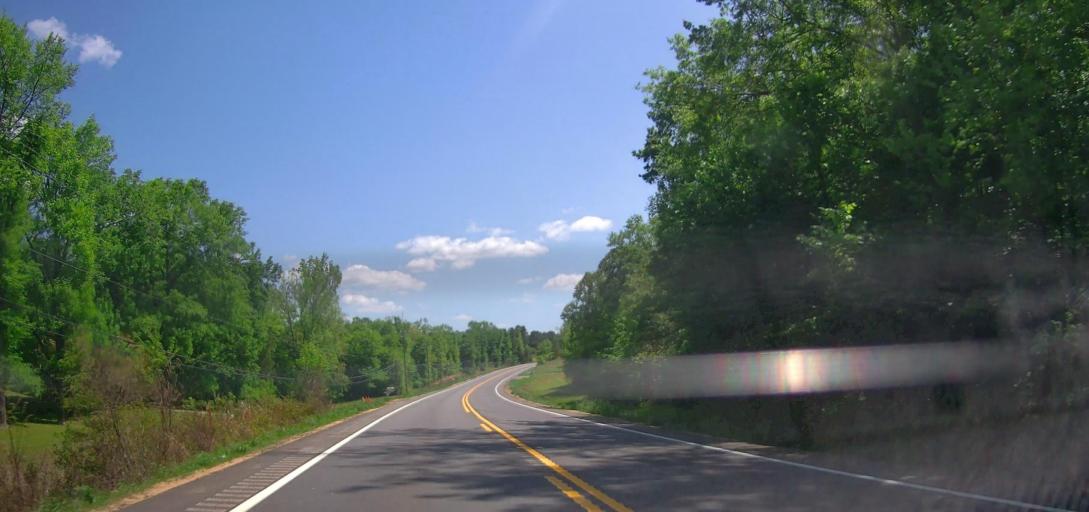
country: US
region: Georgia
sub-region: Putnam County
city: Eatonton
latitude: 33.2290
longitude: -83.4322
